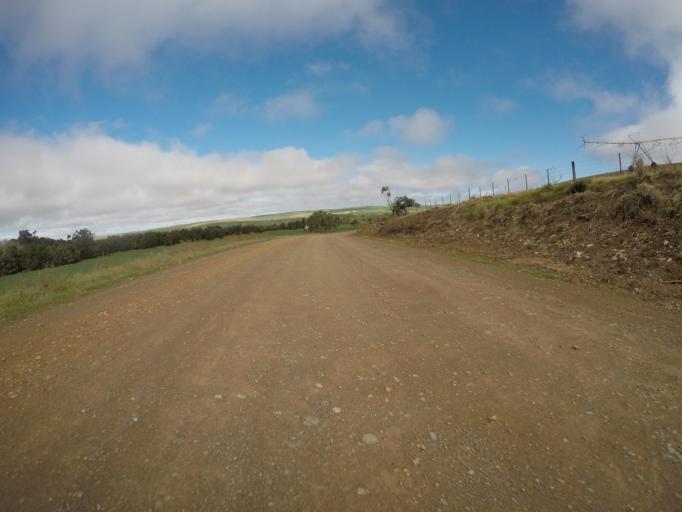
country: ZA
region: Western Cape
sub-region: Overberg District Municipality
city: Caledon
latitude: -34.1158
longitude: 19.7898
